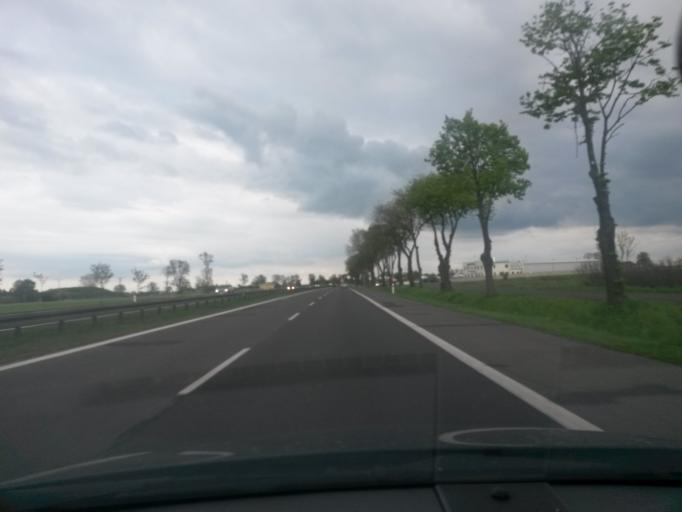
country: PL
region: Masovian Voivodeship
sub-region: Powiat plonski
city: Plonsk
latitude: 52.5937
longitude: 20.4381
